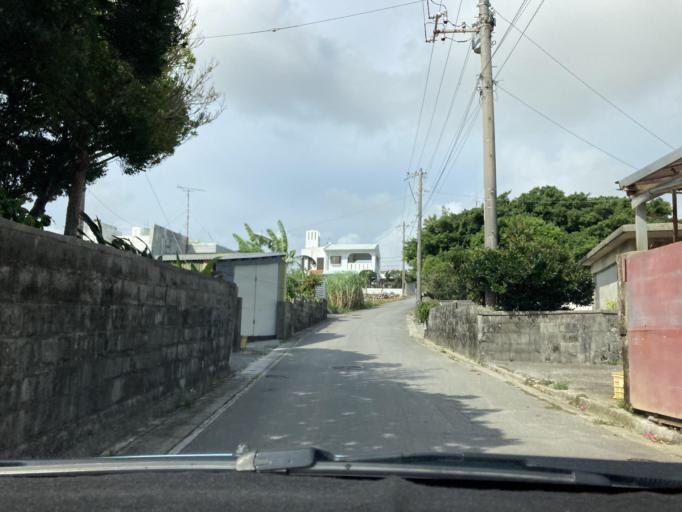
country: JP
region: Okinawa
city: Itoman
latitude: 26.0944
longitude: 127.7046
